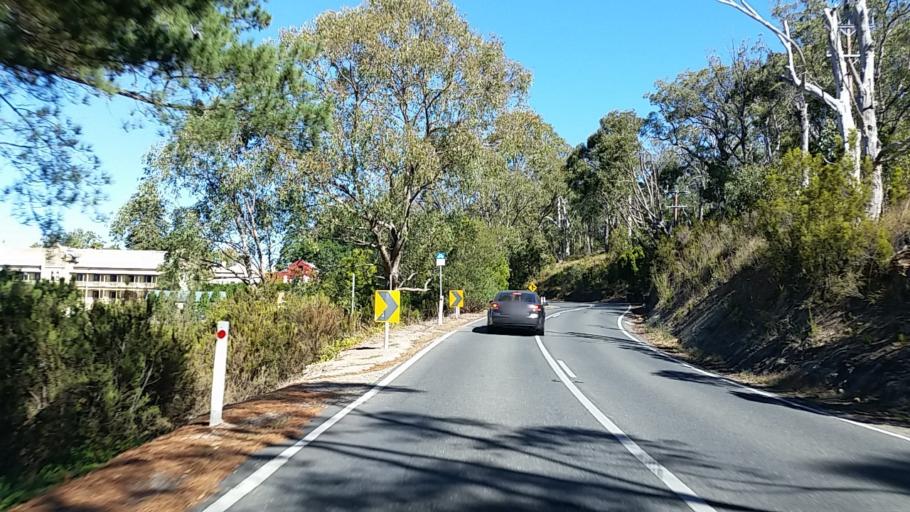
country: AU
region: South Australia
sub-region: Adelaide Hills
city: Crafers
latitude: -34.9851
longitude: 138.7084
